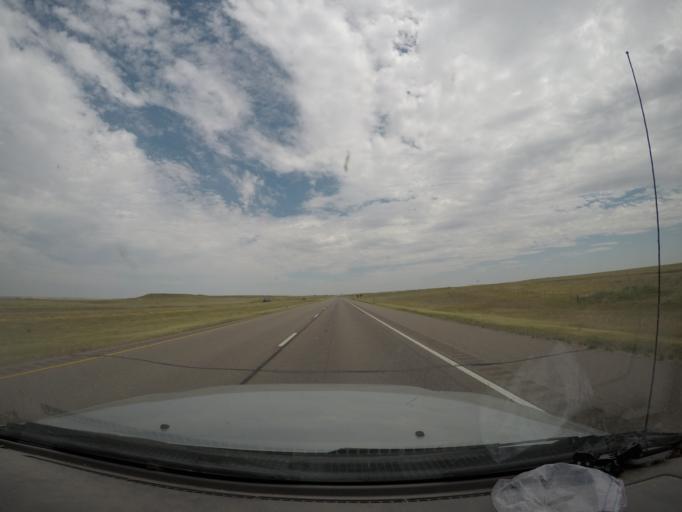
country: US
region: Nebraska
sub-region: Kimball County
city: Kimball
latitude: 41.2070
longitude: -103.7134
